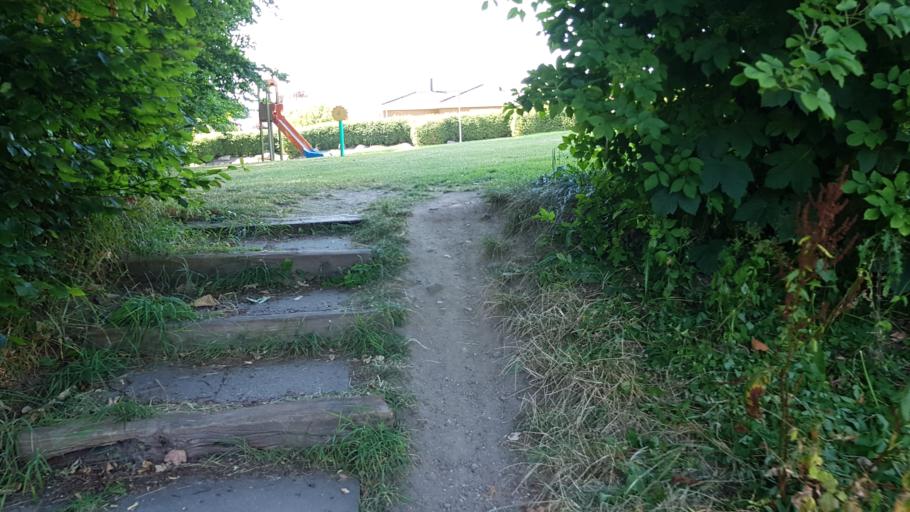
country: DK
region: South Denmark
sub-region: Svendborg Kommune
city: Svendborg
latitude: 55.0453
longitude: 10.5799
